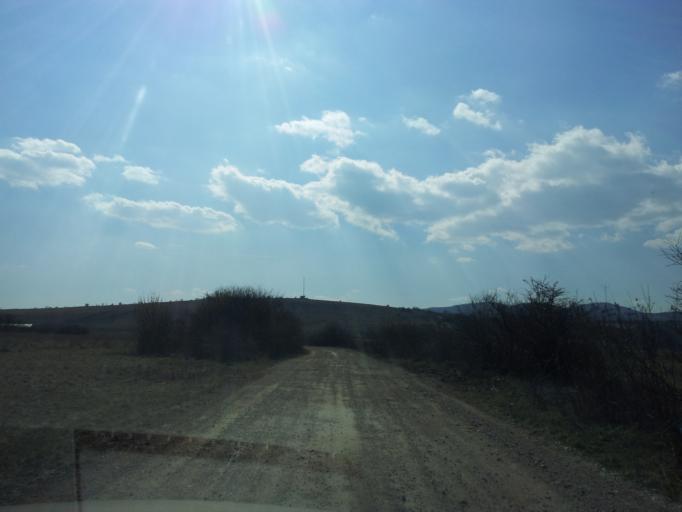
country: HR
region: Zadarska
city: Gracac
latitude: 44.5448
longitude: 15.7486
